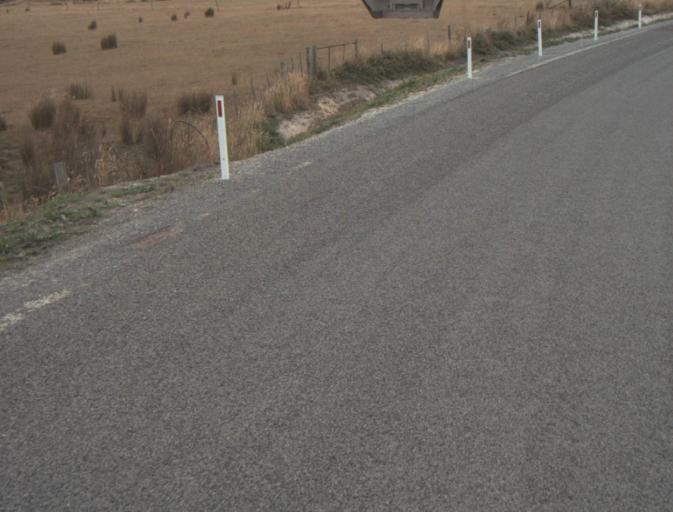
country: AU
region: Tasmania
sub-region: Launceston
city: Mayfield
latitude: -41.1929
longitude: 147.1735
